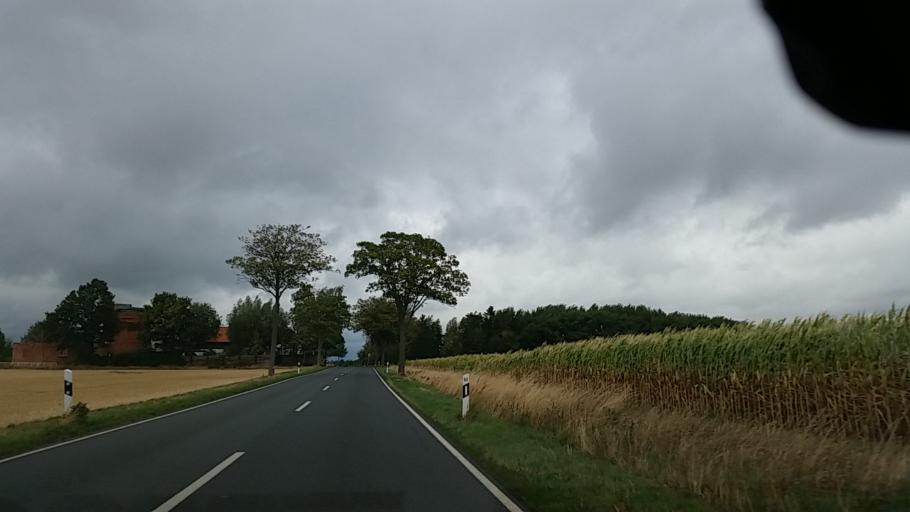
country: DE
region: Lower Saxony
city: Calberlah
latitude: 52.3839
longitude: 10.6453
